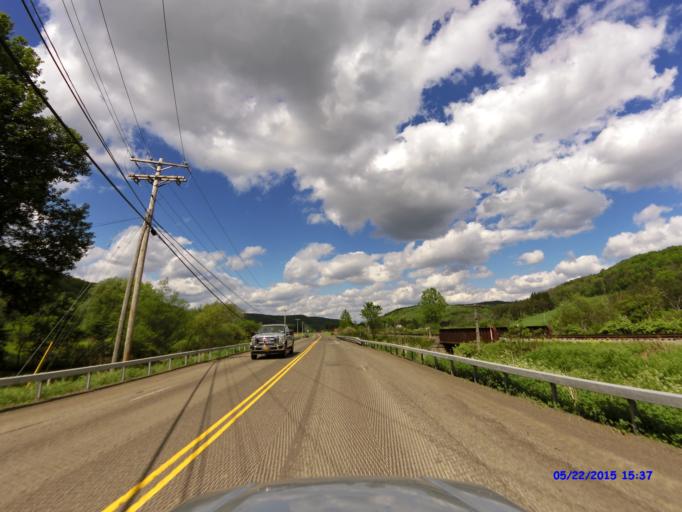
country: US
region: New York
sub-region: Cattaraugus County
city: Salamanca
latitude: 42.3034
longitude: -78.6301
